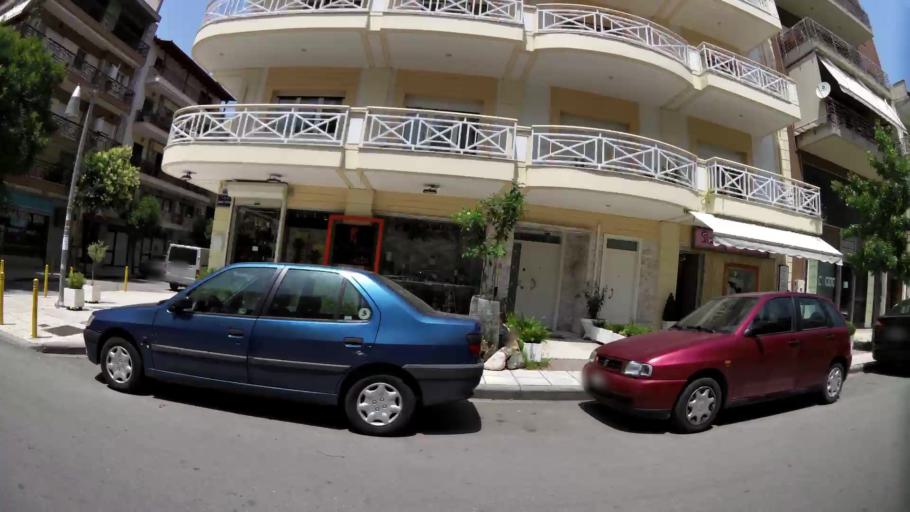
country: GR
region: Central Macedonia
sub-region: Nomos Thessalonikis
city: Evosmos
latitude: 40.6680
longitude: 22.8991
